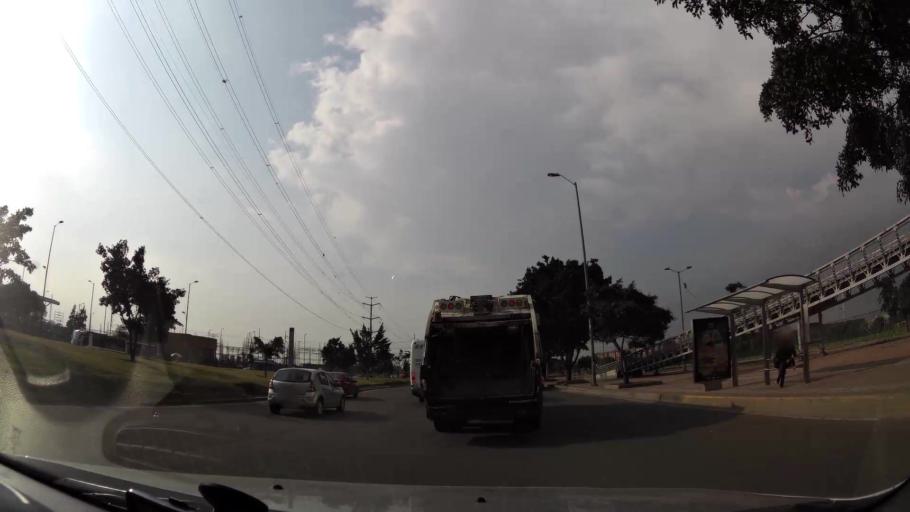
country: CO
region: Bogota D.C.
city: Bogota
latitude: 4.5719
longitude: -74.1391
